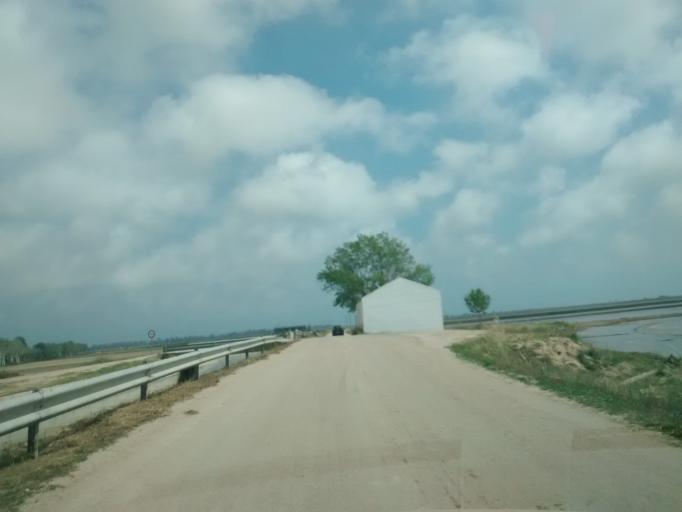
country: ES
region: Catalonia
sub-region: Provincia de Tarragona
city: Deltebre
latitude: 40.6932
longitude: 0.7973
